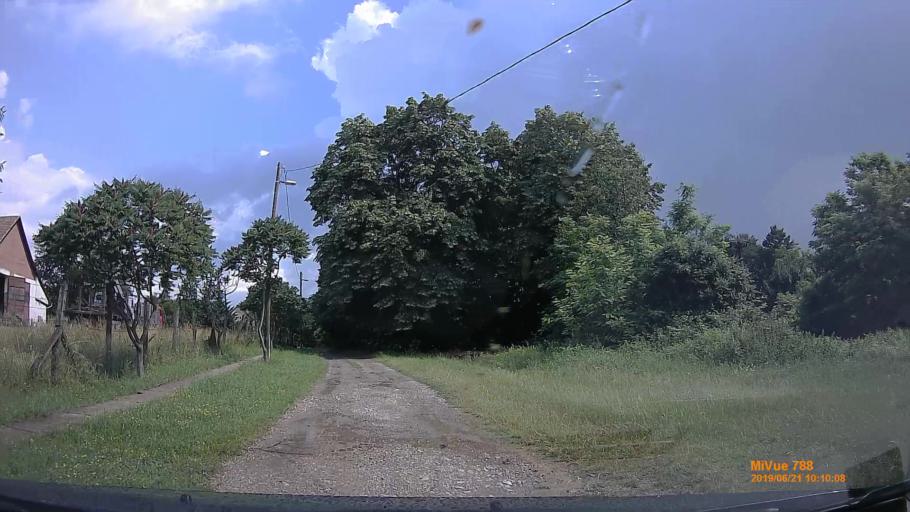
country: HU
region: Baranya
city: Buekkoesd
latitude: 46.1944
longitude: 17.9568
